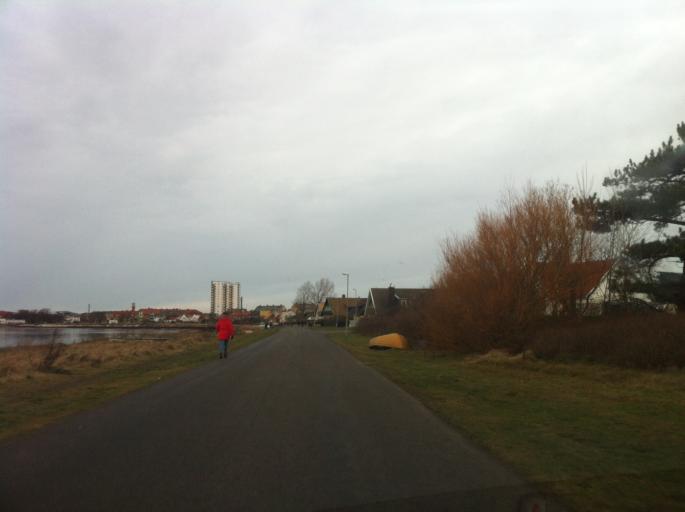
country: SE
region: Skane
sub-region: Hoganas Kommun
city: Hoganas
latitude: 56.1933
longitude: 12.5544
